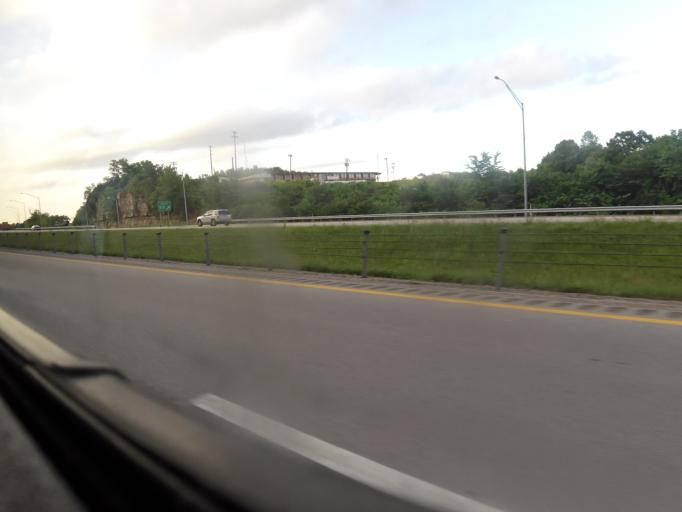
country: US
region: Kentucky
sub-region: Rockcastle County
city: Mount Vernon
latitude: 37.3385
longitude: -84.3069
